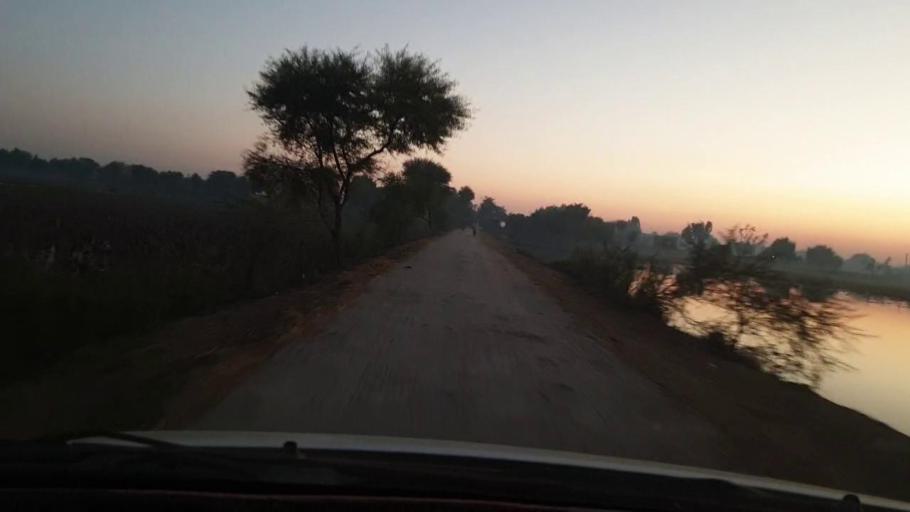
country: PK
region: Sindh
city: Khairpur Nathan Shah
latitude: 27.1396
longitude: 67.7180
